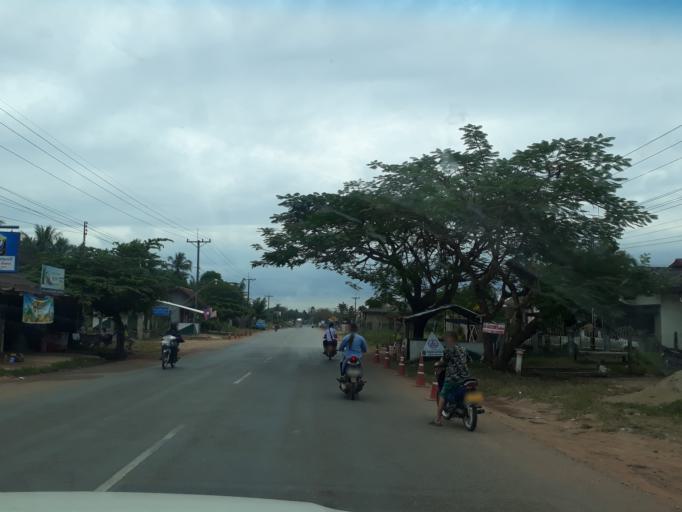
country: LA
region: Vientiane
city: Muang Phon-Hong
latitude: 18.3194
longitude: 102.4536
